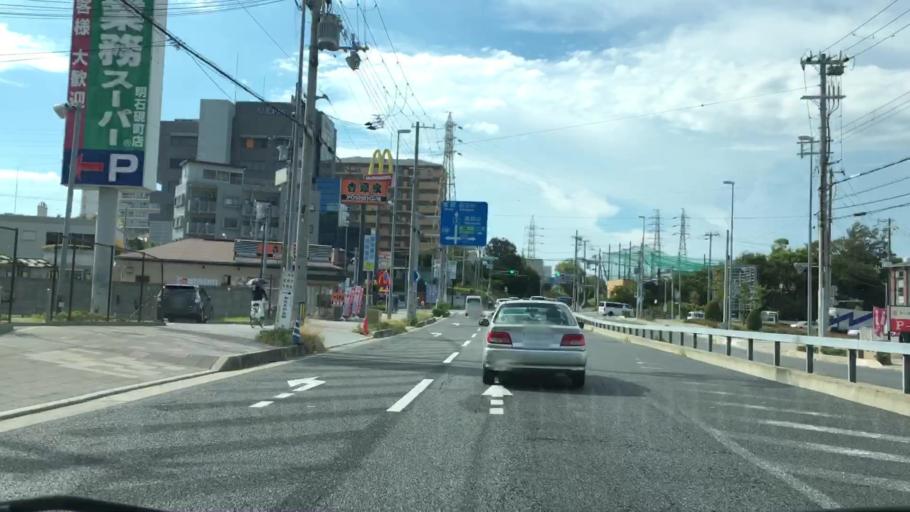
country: JP
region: Hyogo
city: Akashi
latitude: 34.6535
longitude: 134.9759
